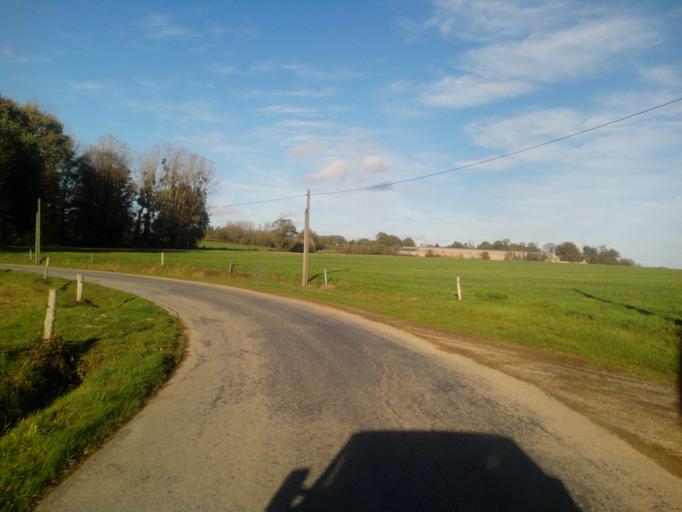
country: FR
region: Brittany
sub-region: Departement du Morbihan
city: Guilliers
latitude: 48.0747
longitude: -2.4087
